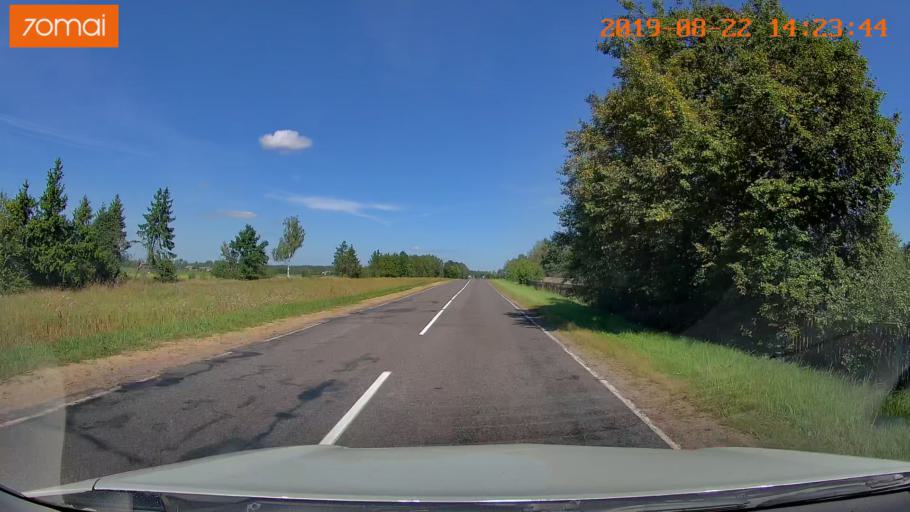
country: BY
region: Mogilev
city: Asipovichy
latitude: 53.2923
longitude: 28.5885
